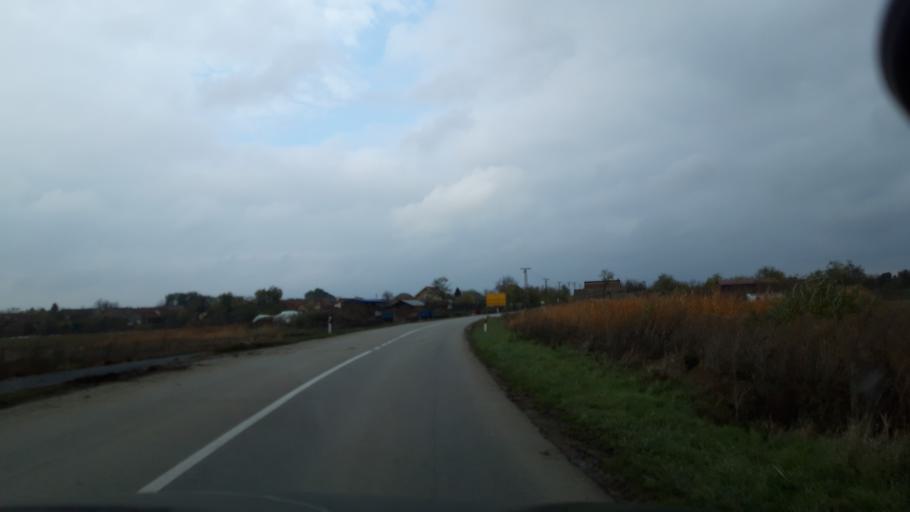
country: RS
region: Autonomna Pokrajina Vojvodina
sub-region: Severnobanatski Okrug
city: Novi Knezevac
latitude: 46.1212
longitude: 20.0981
